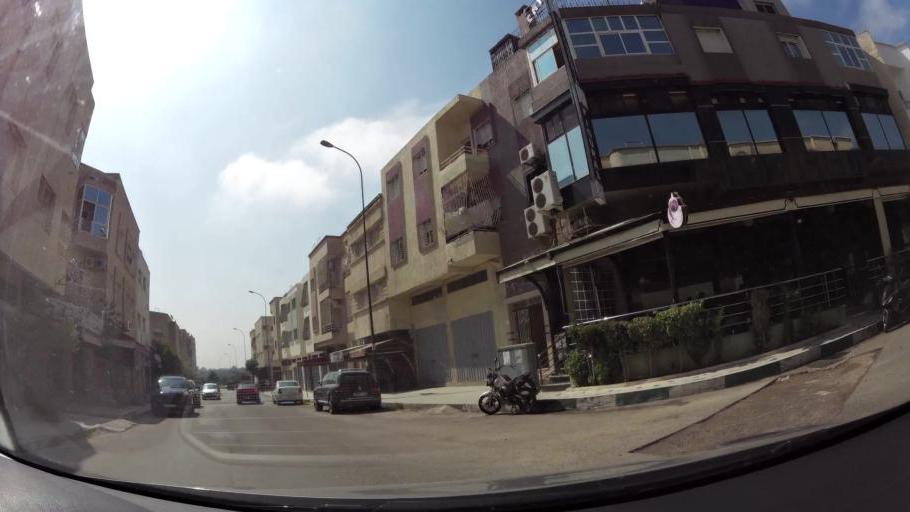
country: MA
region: Fes-Boulemane
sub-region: Fes
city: Fes
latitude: 34.0551
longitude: -5.0285
